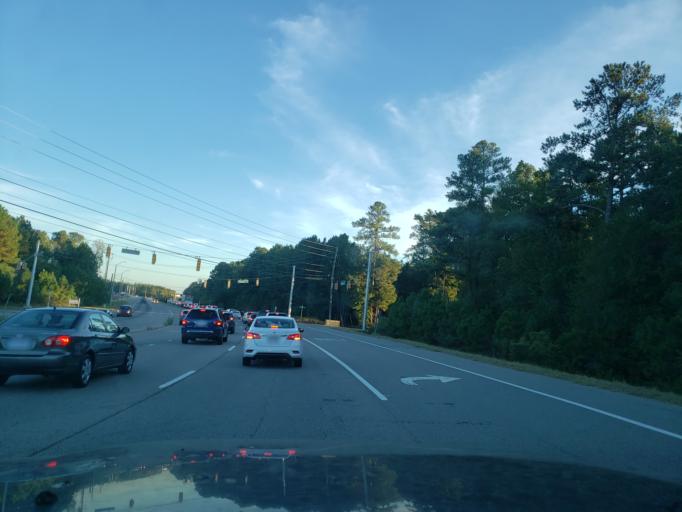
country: US
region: North Carolina
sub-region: Wake County
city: Morrisville
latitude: 35.8294
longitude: -78.8529
